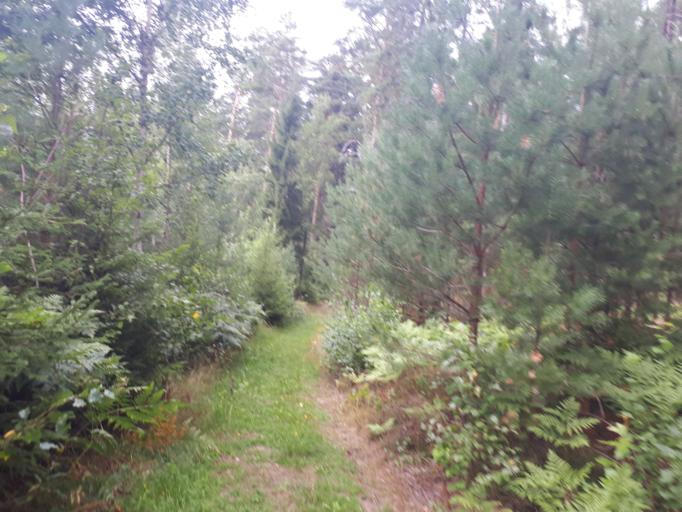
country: SE
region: Soedermanland
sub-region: Flens Kommun
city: Halleforsnas
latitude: 59.0678
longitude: 16.3942
